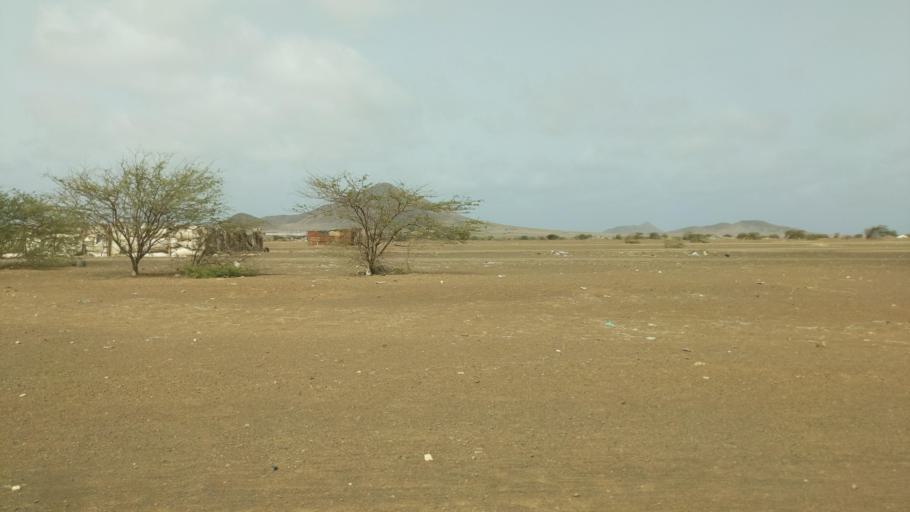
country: CV
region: Sal
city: Espargos
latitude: 16.7707
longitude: -22.9462
